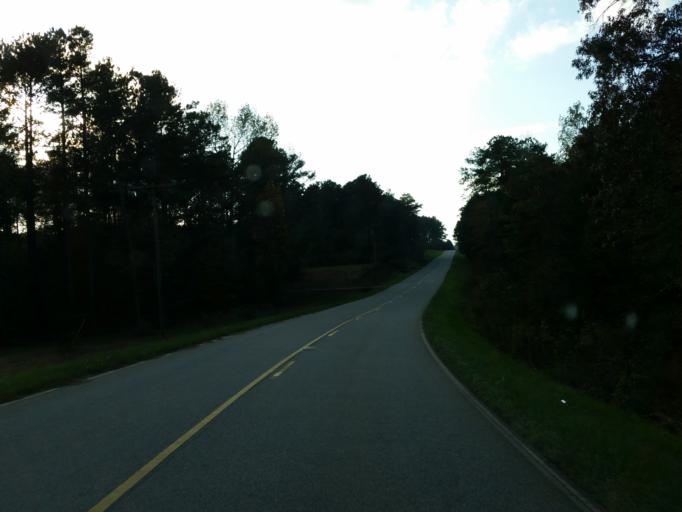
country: US
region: Georgia
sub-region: Monroe County
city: Forsyth
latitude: 32.9786
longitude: -83.8633
